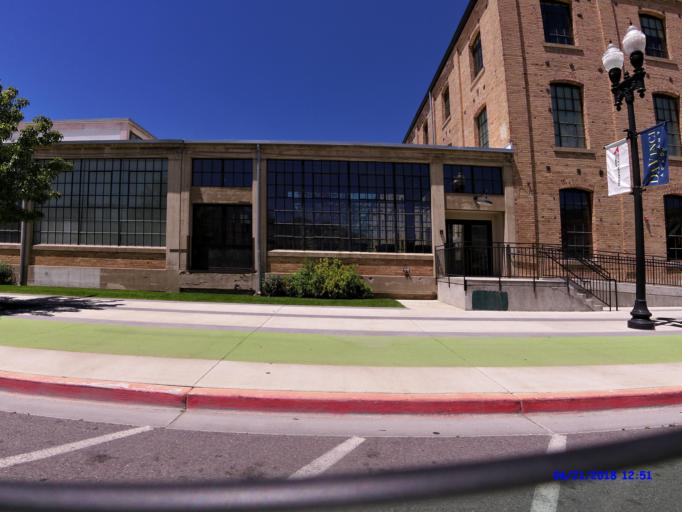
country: US
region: Utah
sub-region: Weber County
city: Ogden
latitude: 41.2308
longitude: -111.9732
